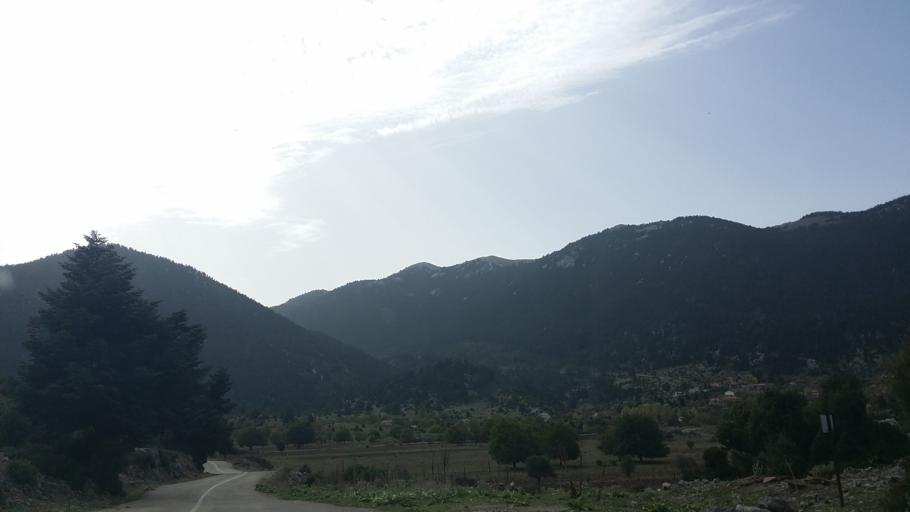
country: GR
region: Central Greece
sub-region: Nomos Voiotias
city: Livadeia
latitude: 38.3742
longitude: 22.8461
